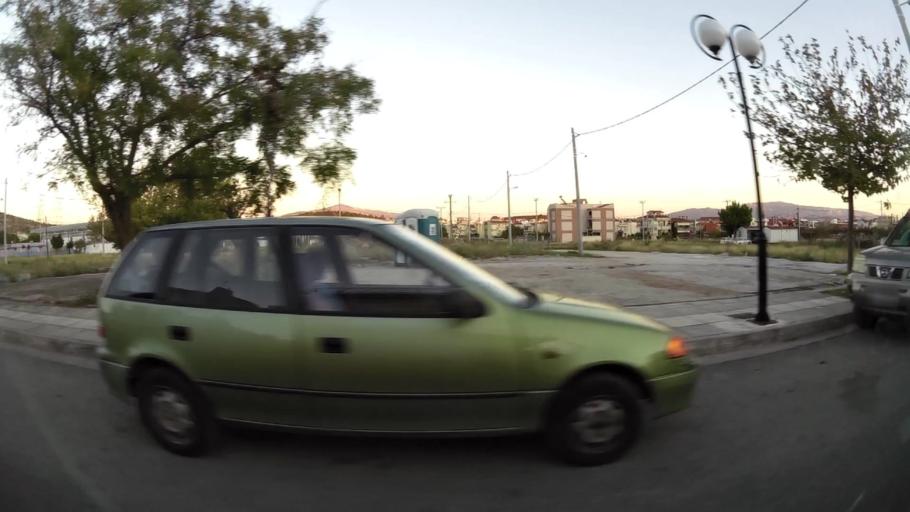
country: GR
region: Attica
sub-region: Nomarchia Dytikis Attikis
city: Ano Liosia
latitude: 38.0889
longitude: 23.7092
